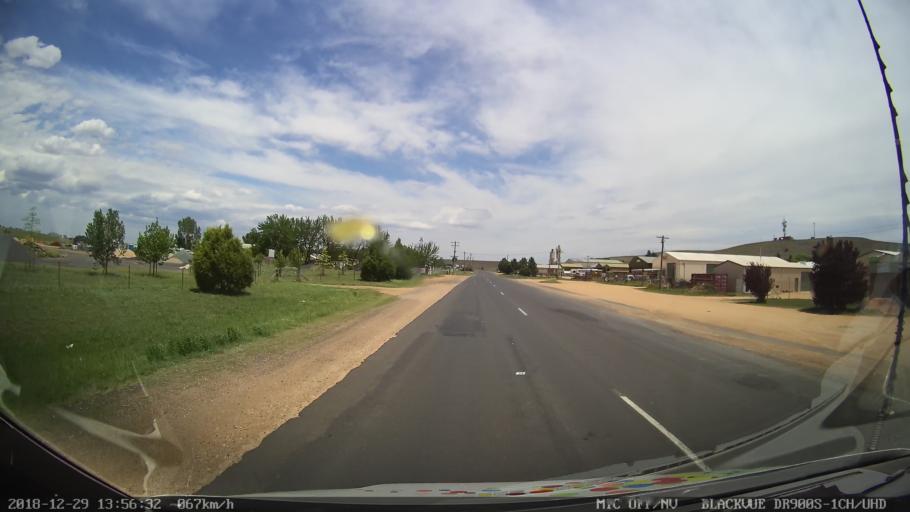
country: AU
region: New South Wales
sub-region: Cooma-Monaro
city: Cooma
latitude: -36.2315
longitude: 149.1460
